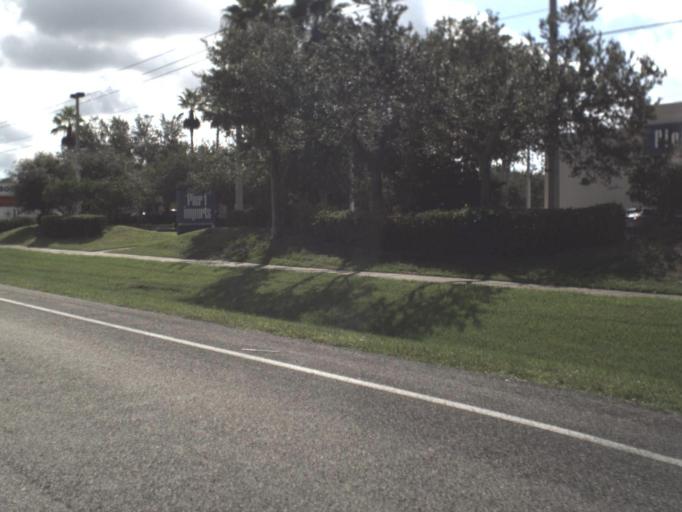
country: US
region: Florida
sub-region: Sarasota County
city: Venice Gardens
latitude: 27.0496
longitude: -82.3948
